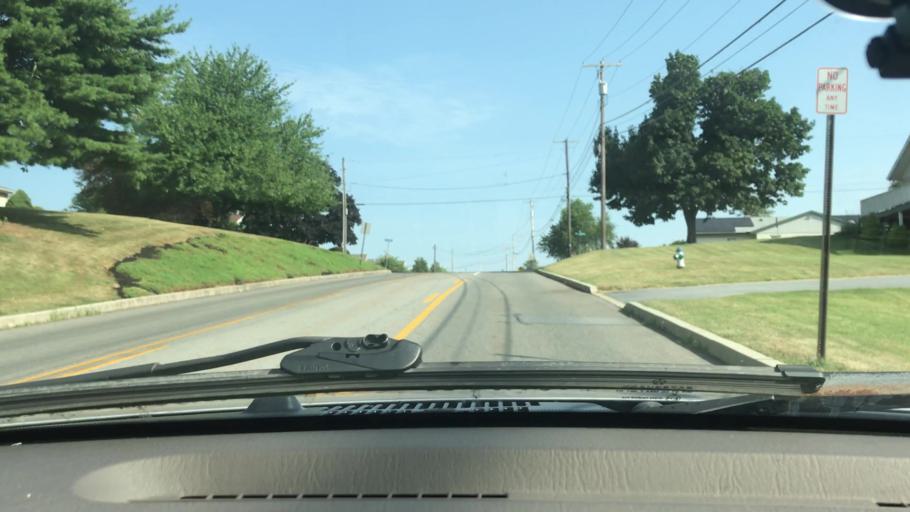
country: US
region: Pennsylvania
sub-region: Lancaster County
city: Rheems
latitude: 40.1395
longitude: -76.5637
